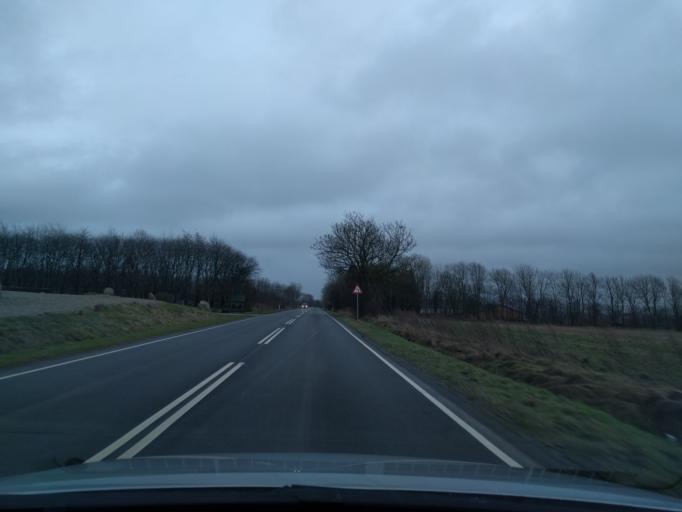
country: DK
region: South Denmark
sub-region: Haderslev Kommune
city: Vojens
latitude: 55.2430
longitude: 9.2126
